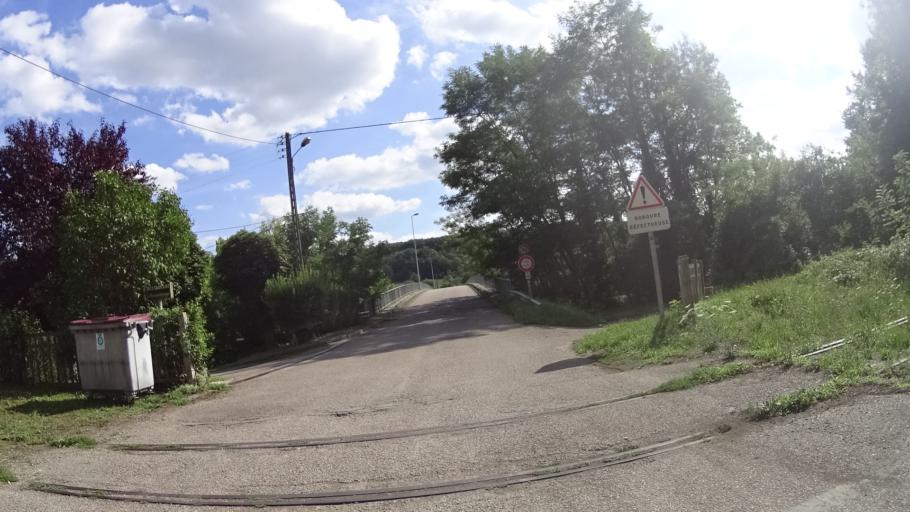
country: FR
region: Lorraine
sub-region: Departement de Meurthe-et-Moselle
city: Dommartin-les-Toul
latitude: 48.6459
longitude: 5.9345
